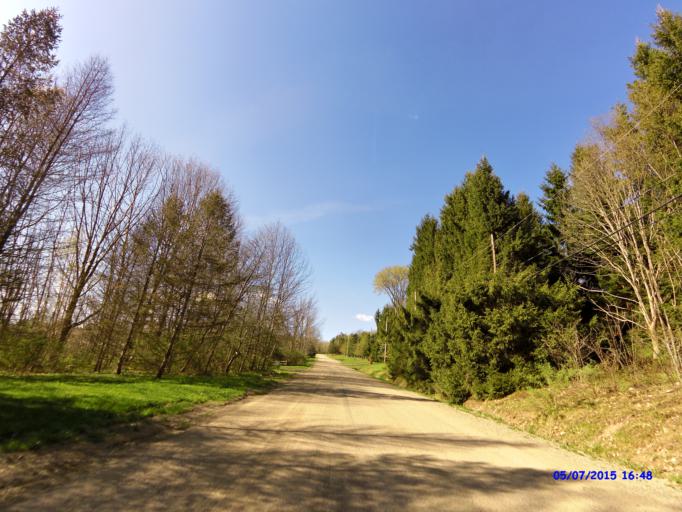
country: US
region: New York
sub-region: Cattaraugus County
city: Little Valley
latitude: 42.2797
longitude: -78.6984
